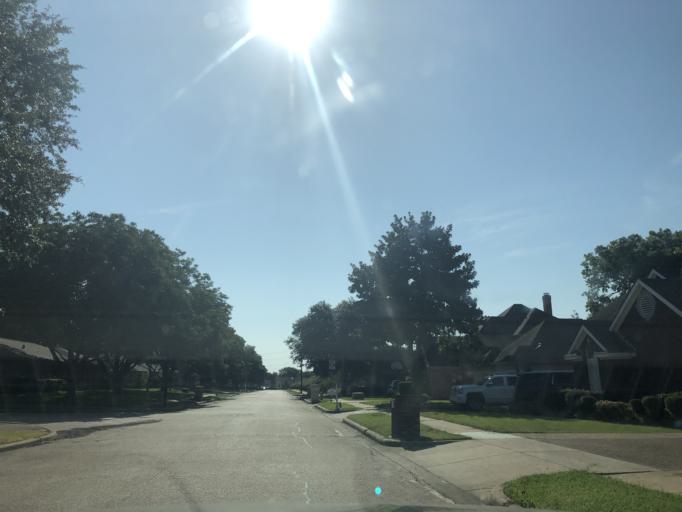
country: US
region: Texas
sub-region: Dallas County
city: Garland
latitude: 32.8642
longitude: -96.6423
